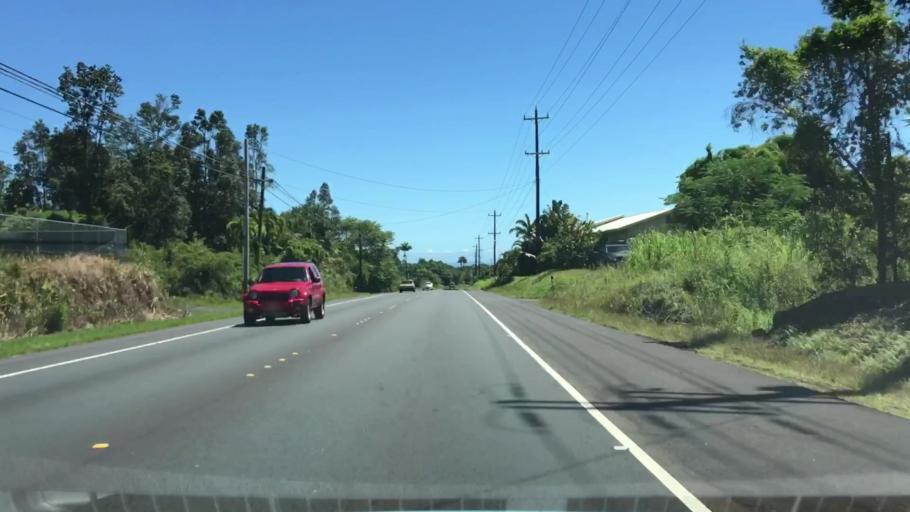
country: US
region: Hawaii
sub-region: Hawaii County
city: Mountain View
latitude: 19.5694
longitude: -155.0808
